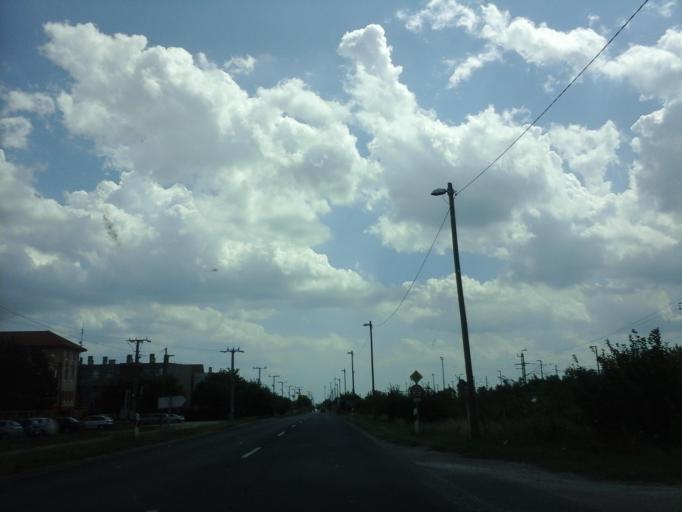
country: HU
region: Gyor-Moson-Sopron
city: Rajka
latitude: 48.0027
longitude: 17.1874
